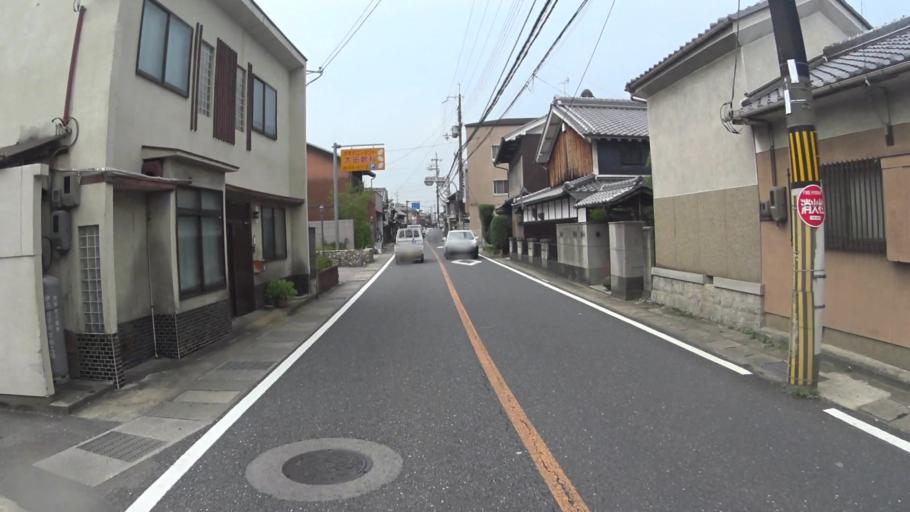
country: JP
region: Kyoto
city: Tanabe
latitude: 34.7921
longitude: 135.7859
